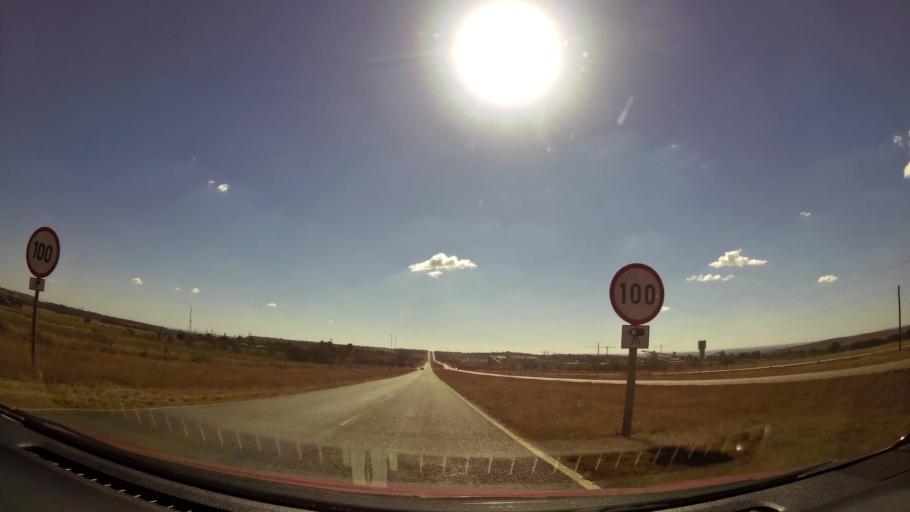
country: ZA
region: Gauteng
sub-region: West Rand District Municipality
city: Carletonville
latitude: -26.4102
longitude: 27.4306
